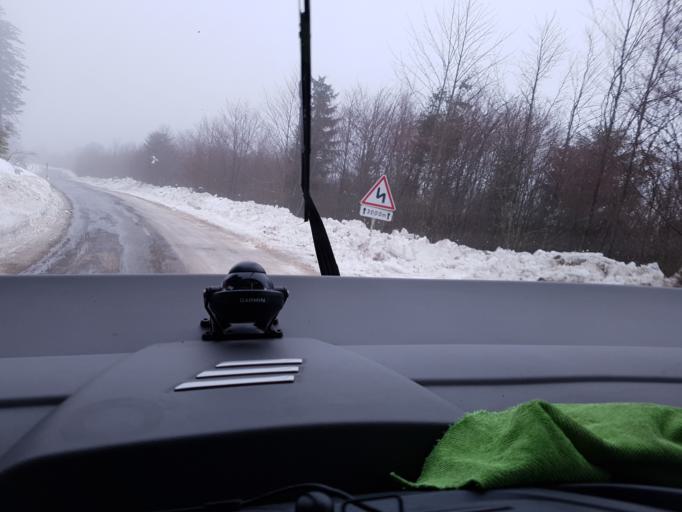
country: FR
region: Lorraine
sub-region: Departement des Vosges
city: Plainfaing
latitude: 48.1369
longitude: 7.0813
